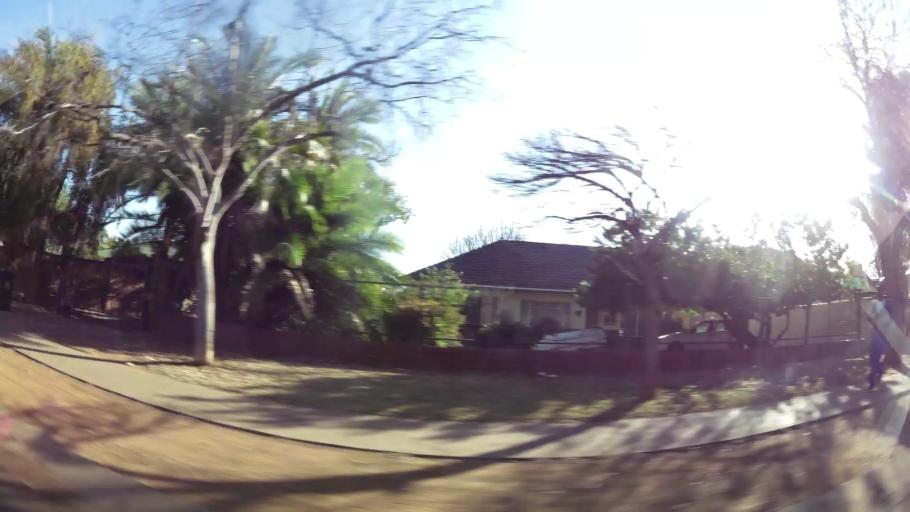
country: ZA
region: Gauteng
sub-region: City of Tshwane Metropolitan Municipality
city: Pretoria
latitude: -25.7102
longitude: 28.2425
